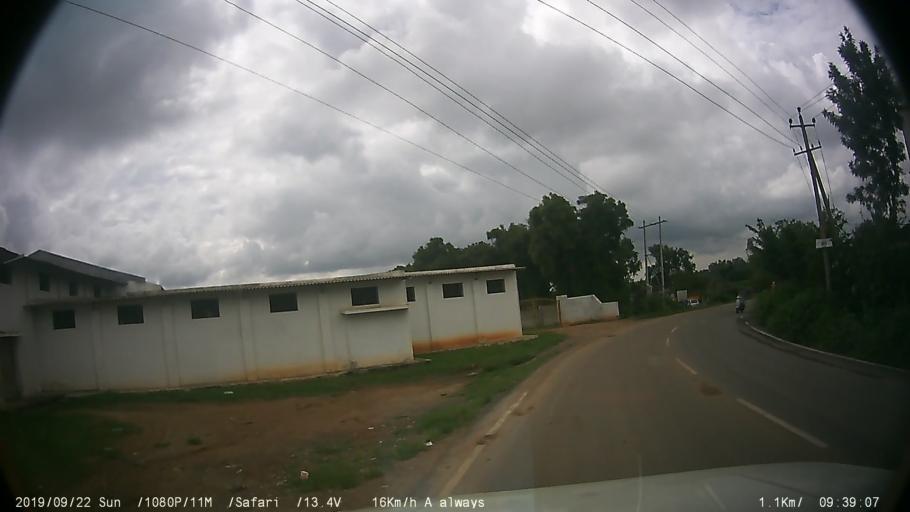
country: IN
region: Karnataka
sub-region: Bangalore Urban
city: Anekal
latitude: 12.8176
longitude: 77.6279
